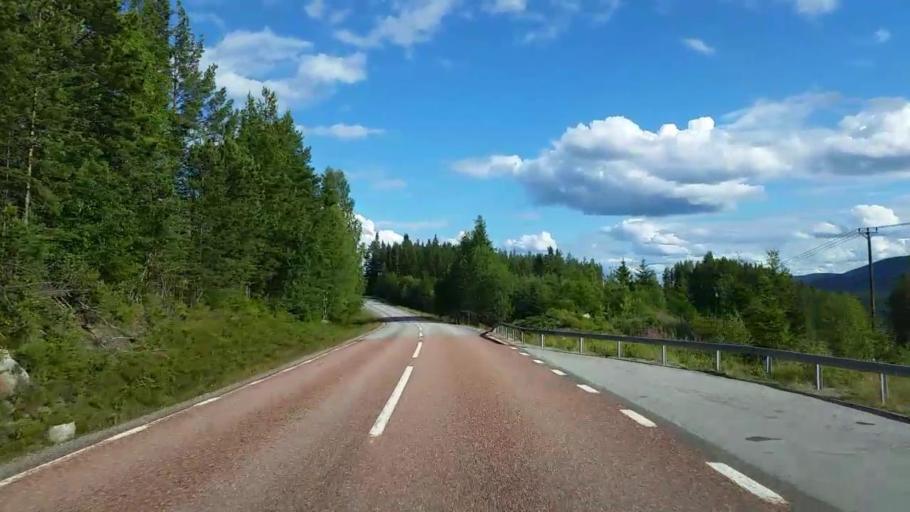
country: SE
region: Gaevleborg
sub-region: Ljusdals Kommun
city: Farila
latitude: 62.1036
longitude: 15.7760
